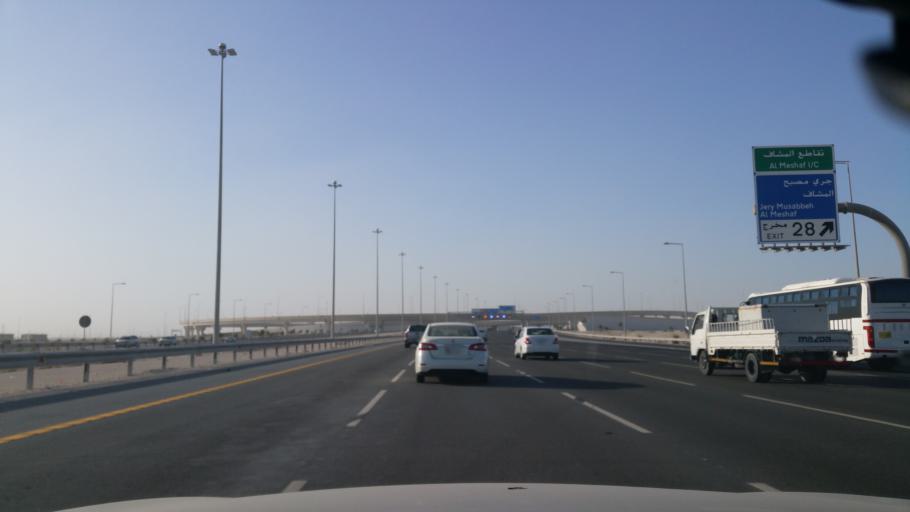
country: QA
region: Al Wakrah
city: Al Wukayr
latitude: 25.1775
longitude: 51.5524
